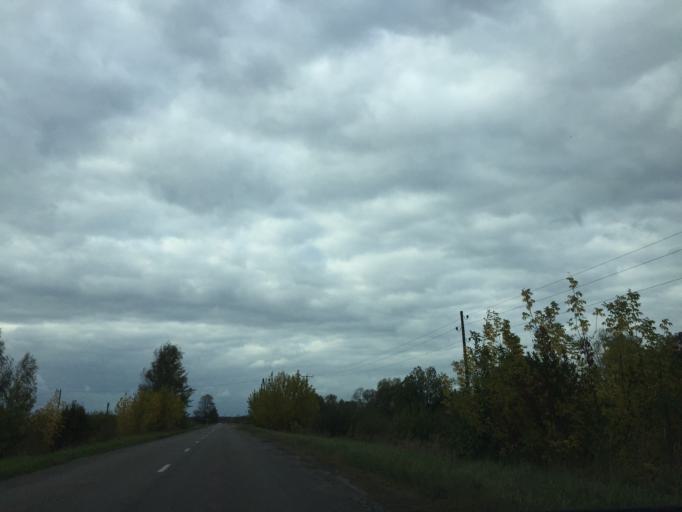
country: LV
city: Tireli
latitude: 56.8048
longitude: 23.5916
